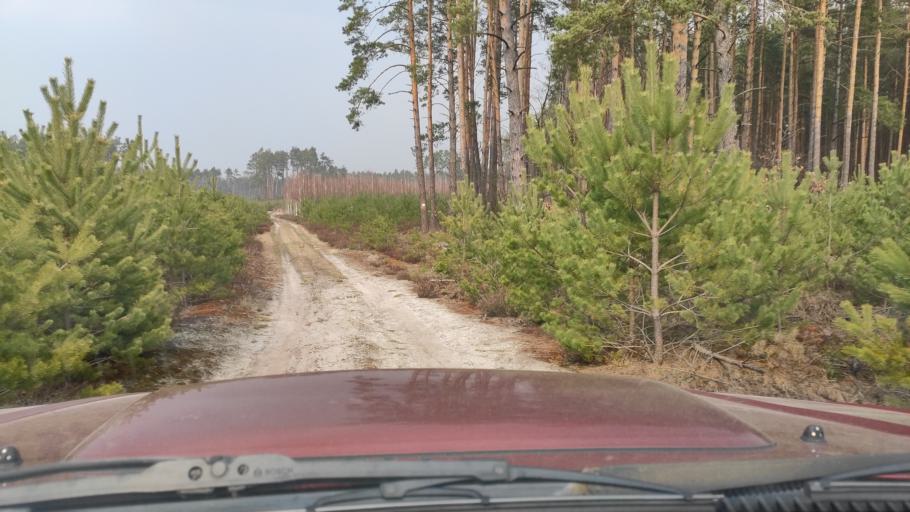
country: PL
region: Masovian Voivodeship
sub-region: Powiat zwolenski
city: Zwolen
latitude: 51.3906
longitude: 21.5715
